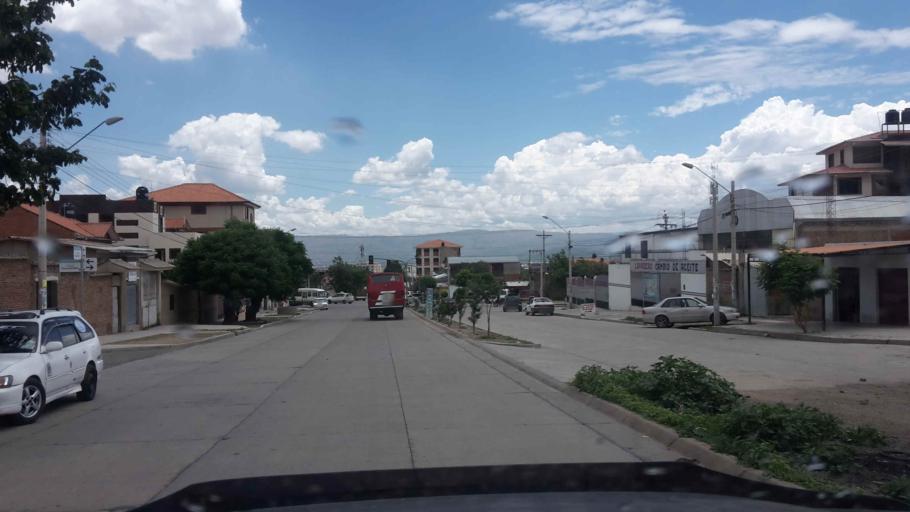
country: BO
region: Cochabamba
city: Cochabamba
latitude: -17.3512
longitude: -66.1822
